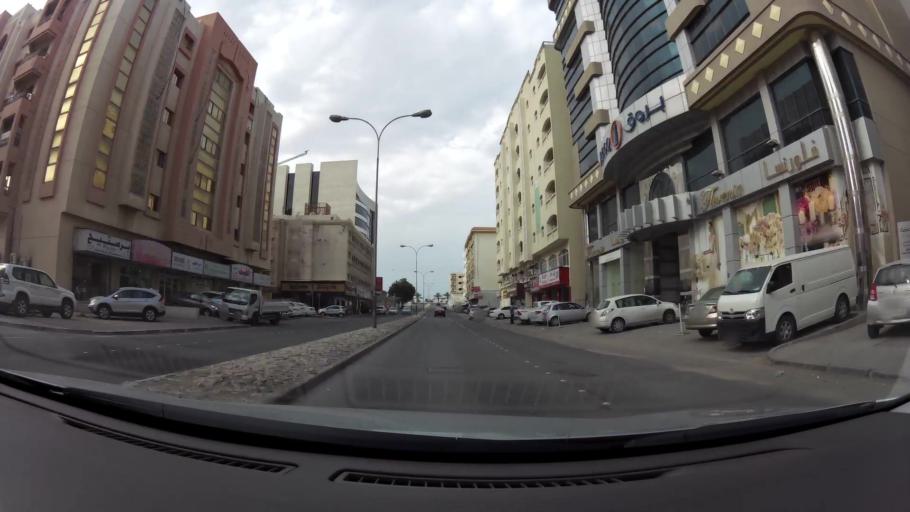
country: QA
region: Baladiyat ad Dawhah
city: Doha
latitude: 25.2872
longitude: 51.5138
